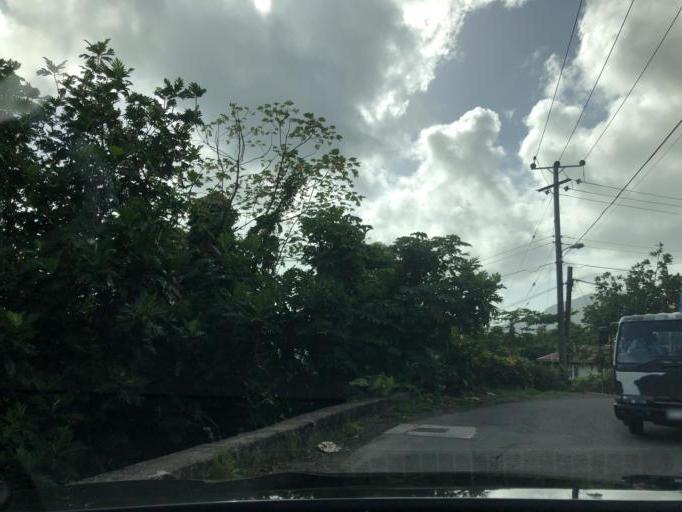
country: LC
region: Castries Quarter
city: Bisee
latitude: 14.0004
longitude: -60.9488
